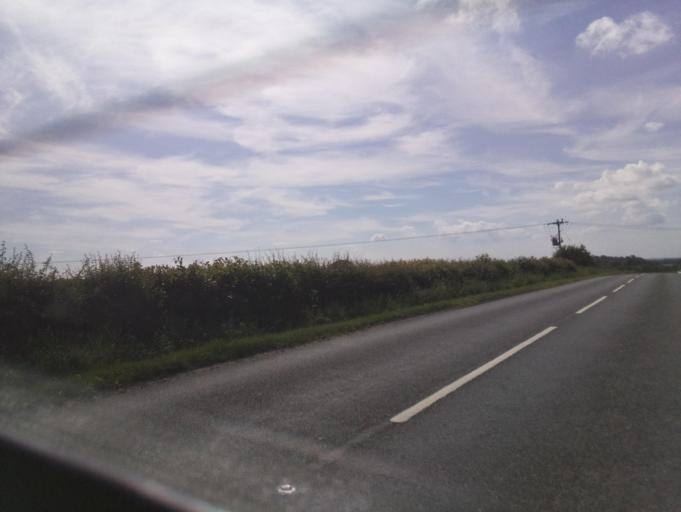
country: GB
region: England
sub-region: Lincolnshire
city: Skellingthorpe
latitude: 53.1620
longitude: -0.6387
